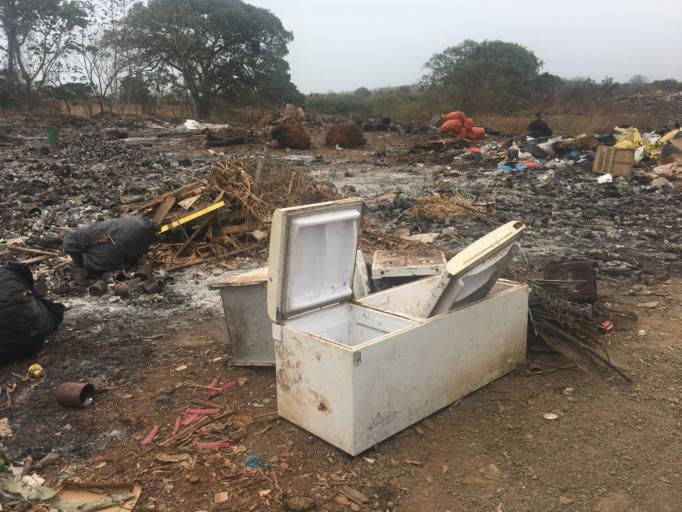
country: PA
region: Los Santos
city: Pedasi
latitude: 7.5483
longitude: -80.0830
